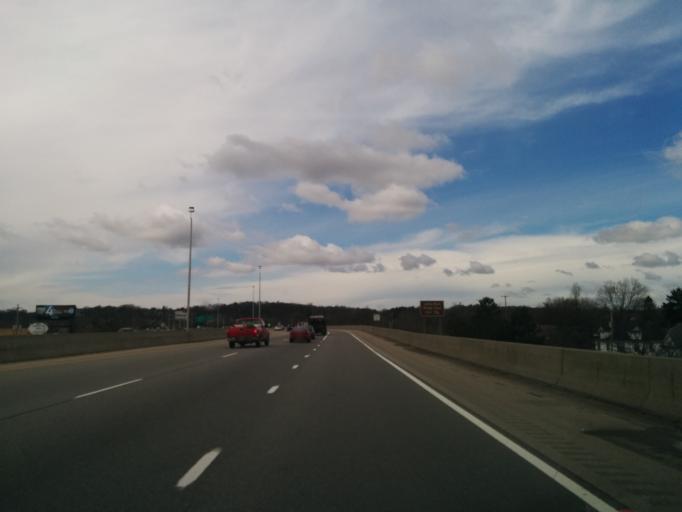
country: US
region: Michigan
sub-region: Kent County
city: Grand Rapids
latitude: 42.9735
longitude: -85.6830
